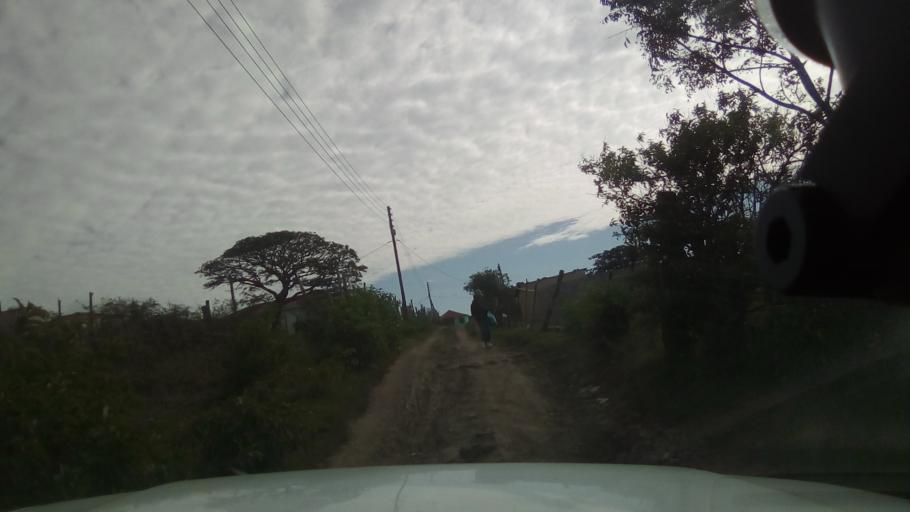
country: ZA
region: Eastern Cape
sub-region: Buffalo City Metropolitan Municipality
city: East London
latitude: -32.7949
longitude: 27.9568
